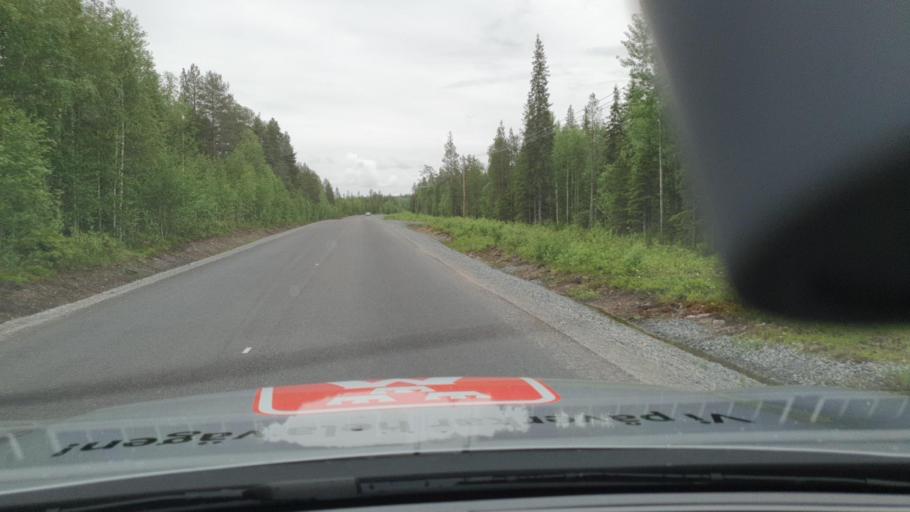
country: SE
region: Norrbotten
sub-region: Overtornea Kommun
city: OEvertornea
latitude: 66.6327
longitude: 23.2647
